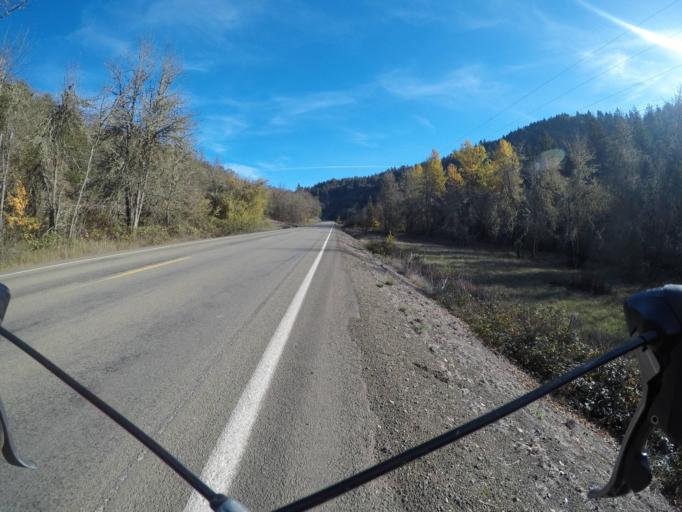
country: US
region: Oregon
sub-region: Douglas County
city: Winston
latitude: 43.1879
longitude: -123.4483
